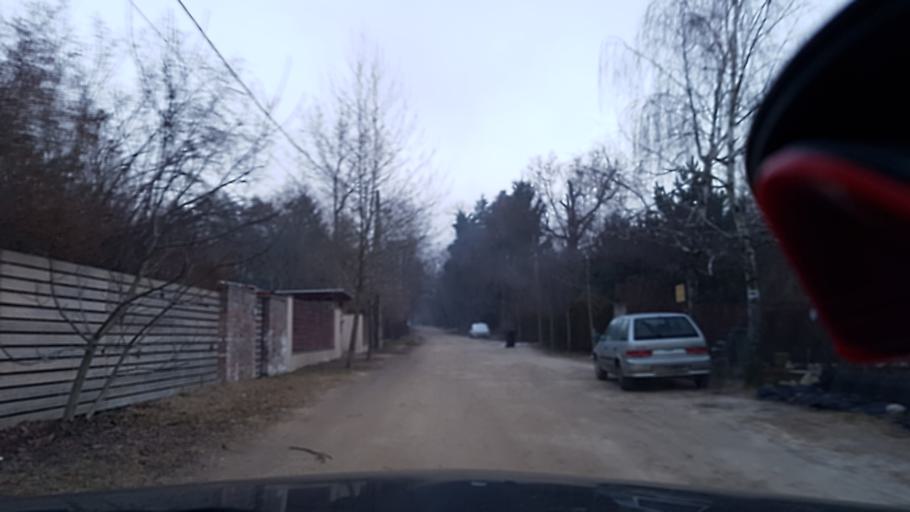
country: HU
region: Pest
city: Piliscsaba
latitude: 47.6418
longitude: 18.8275
